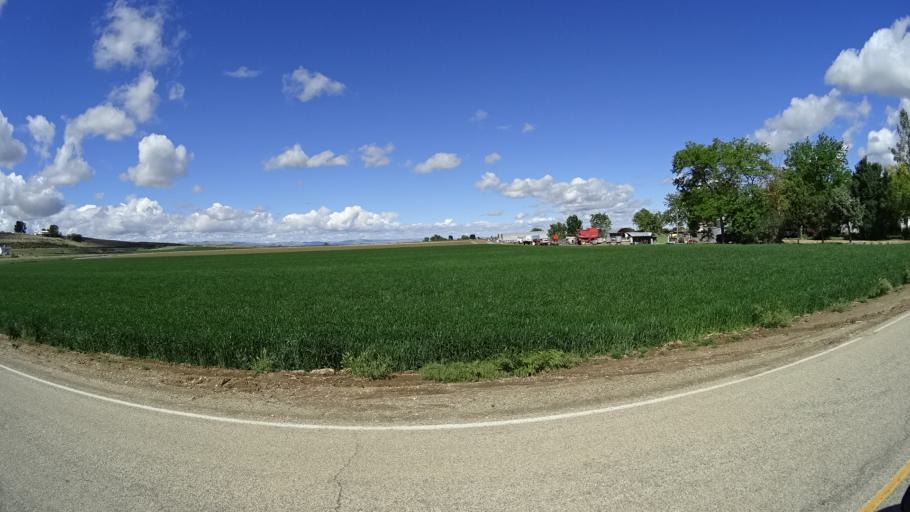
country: US
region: Idaho
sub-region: Ada County
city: Kuna
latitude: 43.4647
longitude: -116.4735
